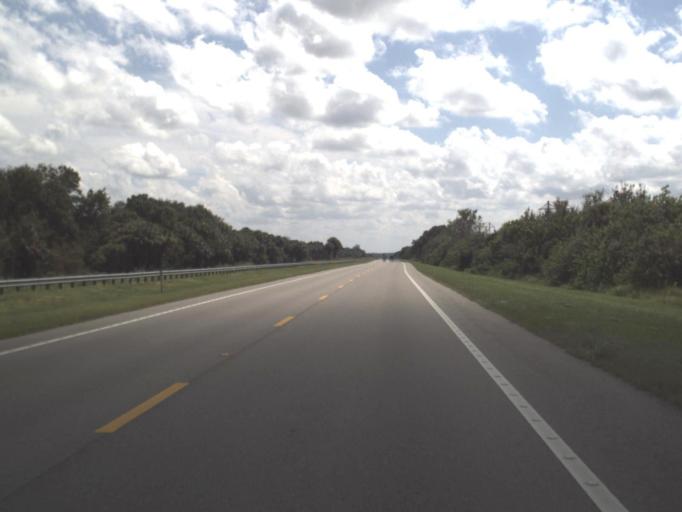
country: US
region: Florida
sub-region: Collier County
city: Immokalee
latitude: 26.3912
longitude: -81.3783
